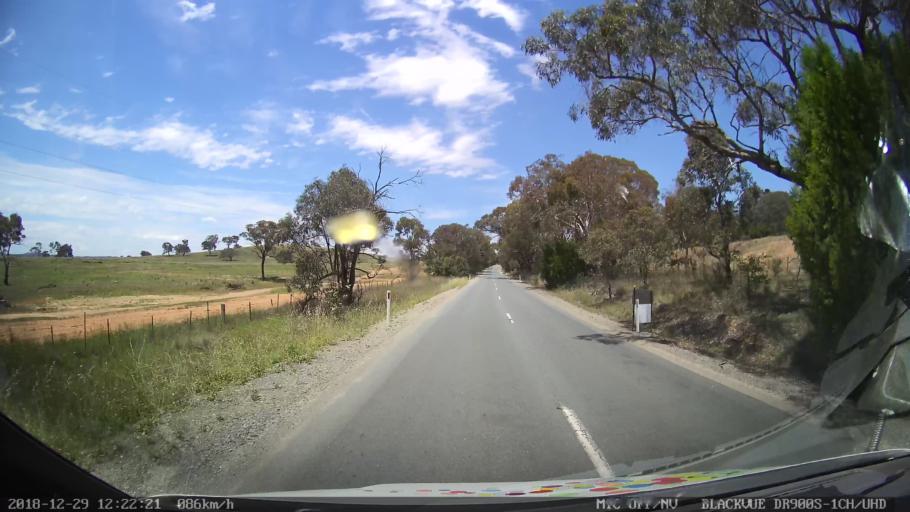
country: AU
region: New South Wales
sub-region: Queanbeyan
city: Queanbeyan
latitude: -35.4236
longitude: 149.2205
